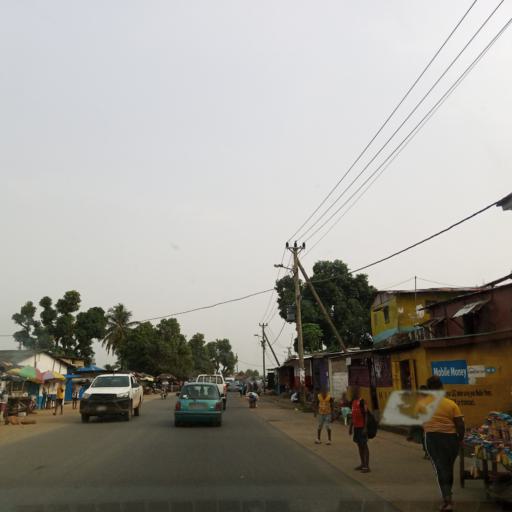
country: LR
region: Montserrado
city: Monrovia
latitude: 6.3033
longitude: -10.7942
